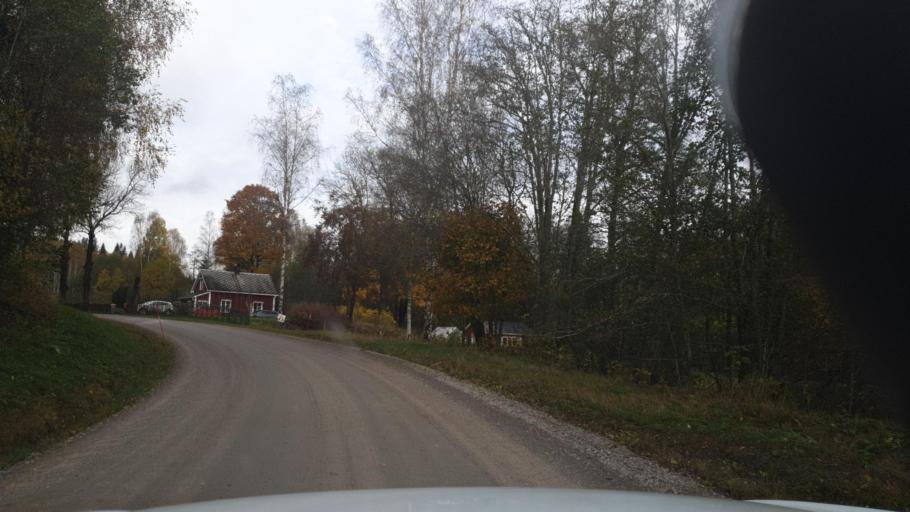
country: SE
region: Vaermland
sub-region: Sunne Kommun
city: Sunne
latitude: 59.6930
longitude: 12.8880
